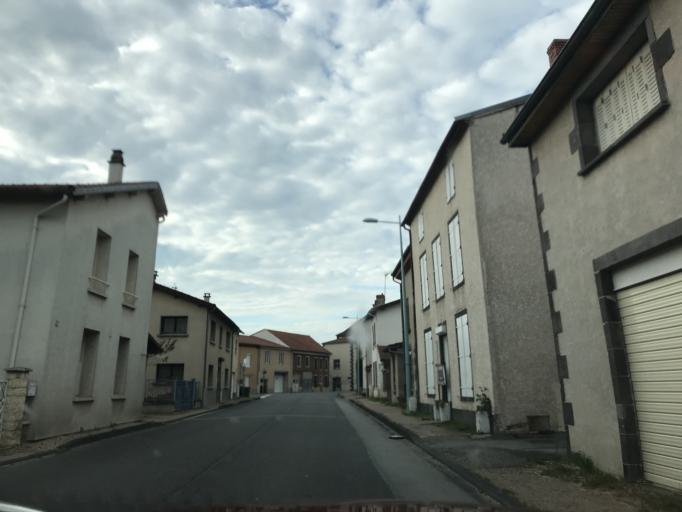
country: FR
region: Auvergne
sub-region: Departement du Puy-de-Dome
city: Randan
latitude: 46.0110
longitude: 3.3520
